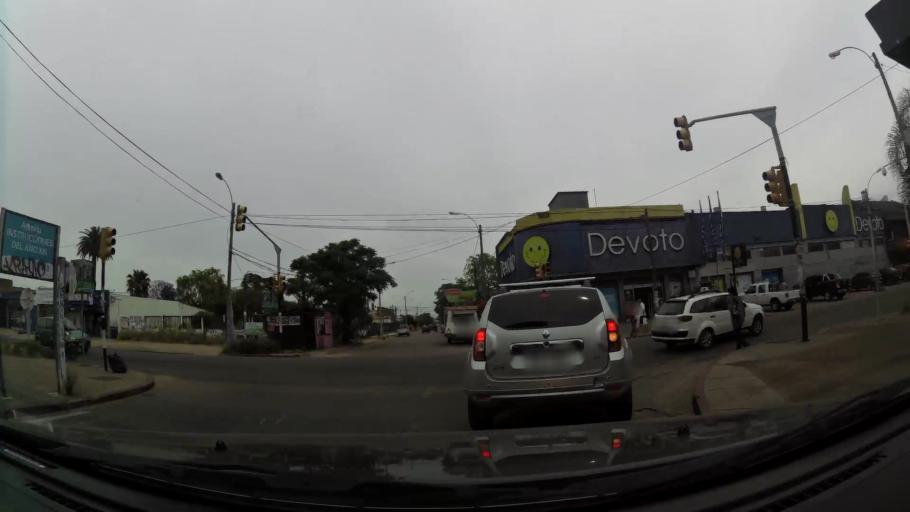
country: UY
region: Canelones
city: Las Piedras
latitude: -34.7281
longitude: -56.2237
